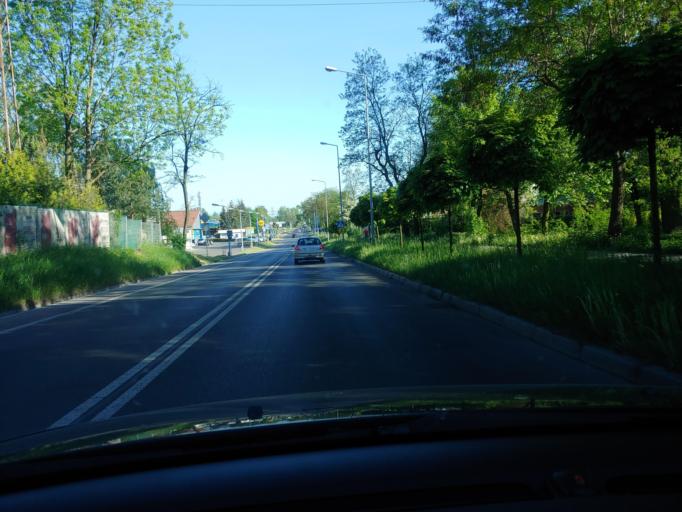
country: PL
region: Silesian Voivodeship
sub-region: Jaworzno
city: Jaworzno
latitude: 50.1954
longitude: 19.2823
